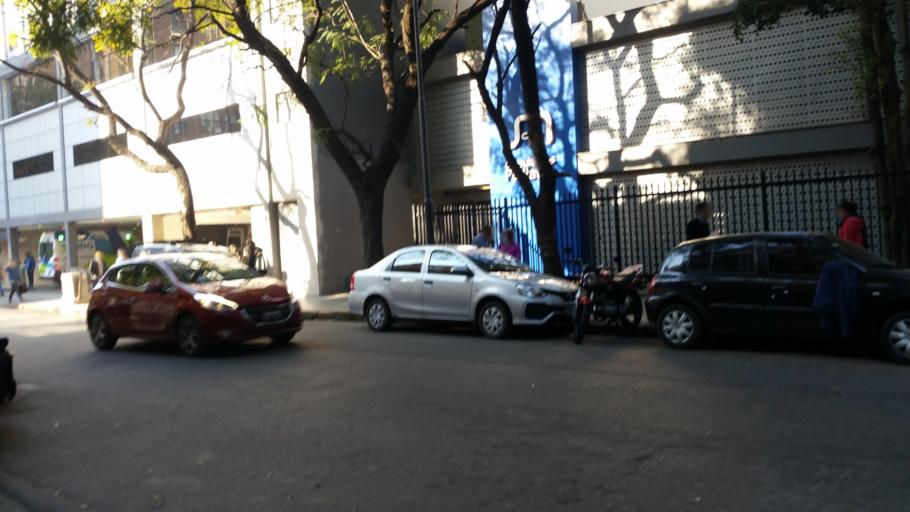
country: AR
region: Cordoba
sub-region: Departamento de Capital
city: Cordoba
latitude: -31.4251
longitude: -64.1877
